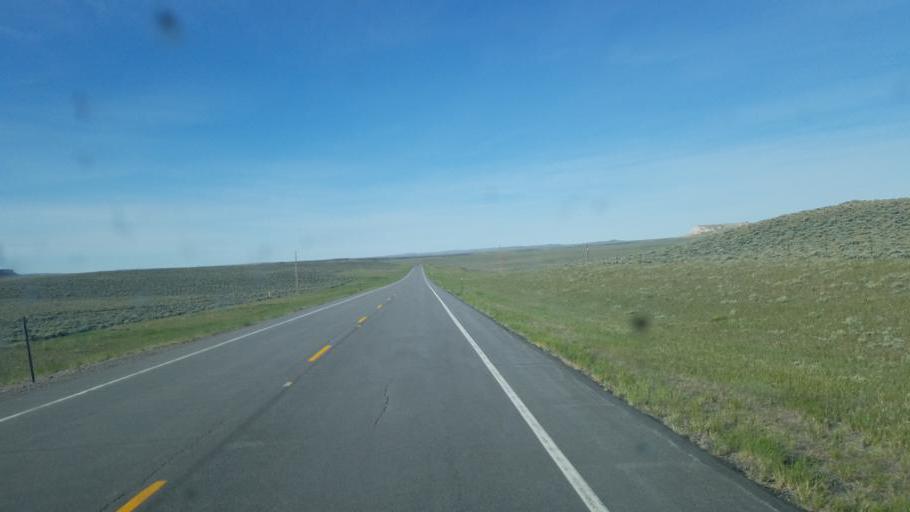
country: US
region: Wyoming
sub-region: Fremont County
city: Riverton
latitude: 42.6586
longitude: -108.1866
